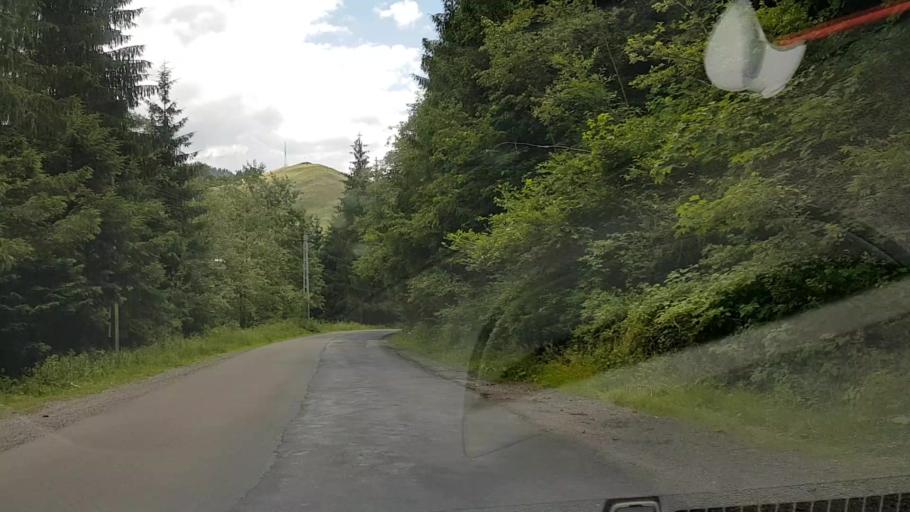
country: RO
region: Suceava
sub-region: Comuna Crucea
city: Crucea
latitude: 47.3499
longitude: 25.6047
